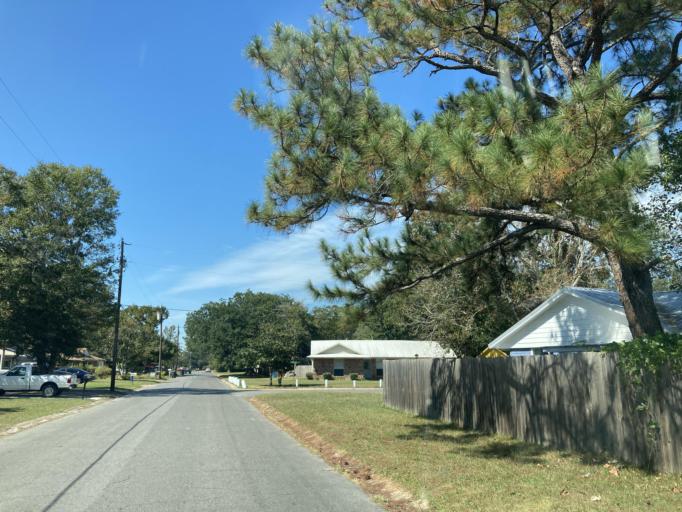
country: US
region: Mississippi
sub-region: Jackson County
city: Saint Martin
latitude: 30.4508
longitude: -88.8718
